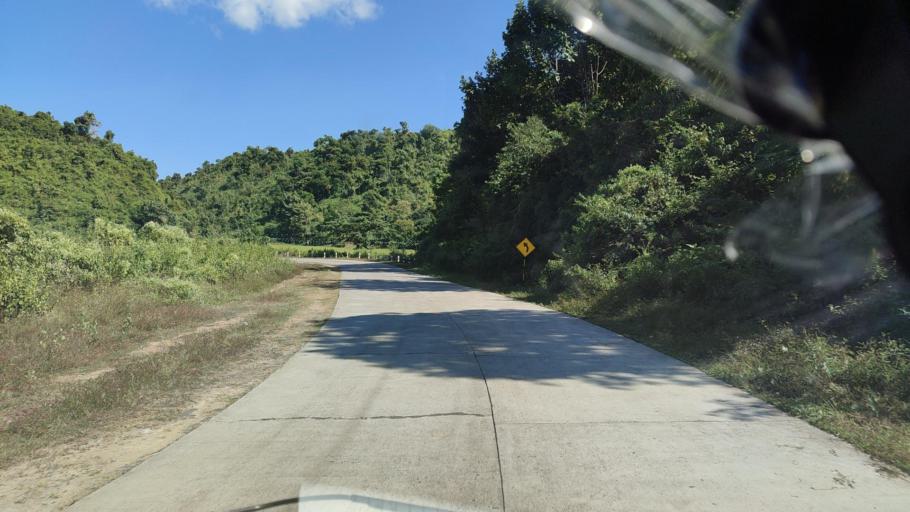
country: MM
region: Rakhine
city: Sittwe
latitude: 20.3189
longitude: 93.3481
